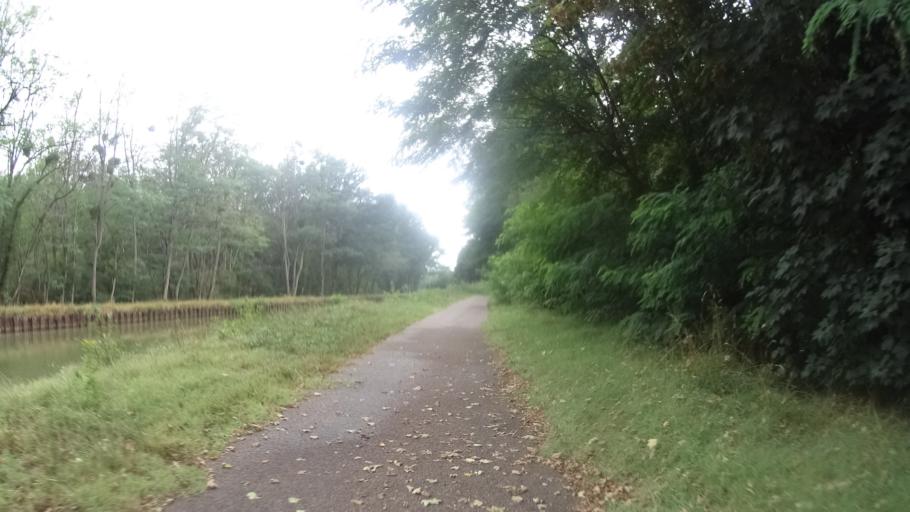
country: FR
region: Bourgogne
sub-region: Departement de la Nievre
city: Saint-Leger-des-Vignes
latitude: 46.8196
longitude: 3.4179
